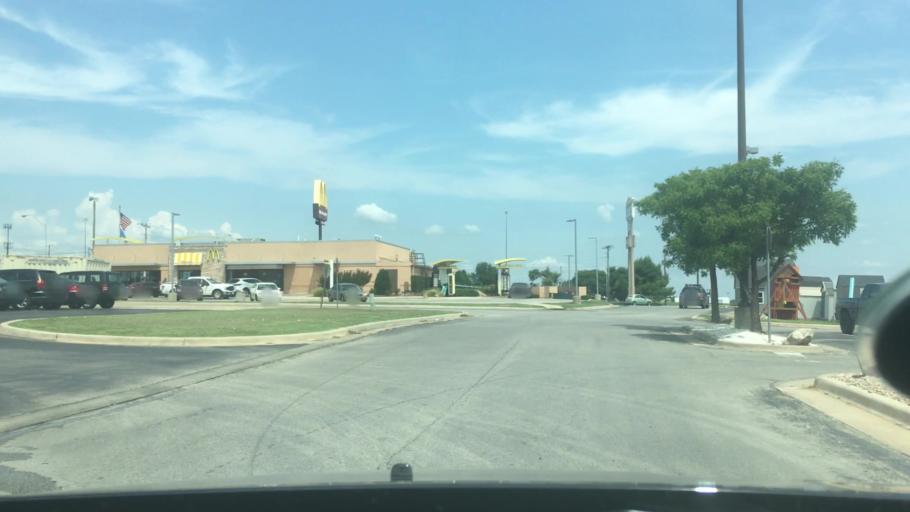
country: US
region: Oklahoma
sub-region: Pottawatomie County
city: Shawnee
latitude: 35.3814
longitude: -96.9287
